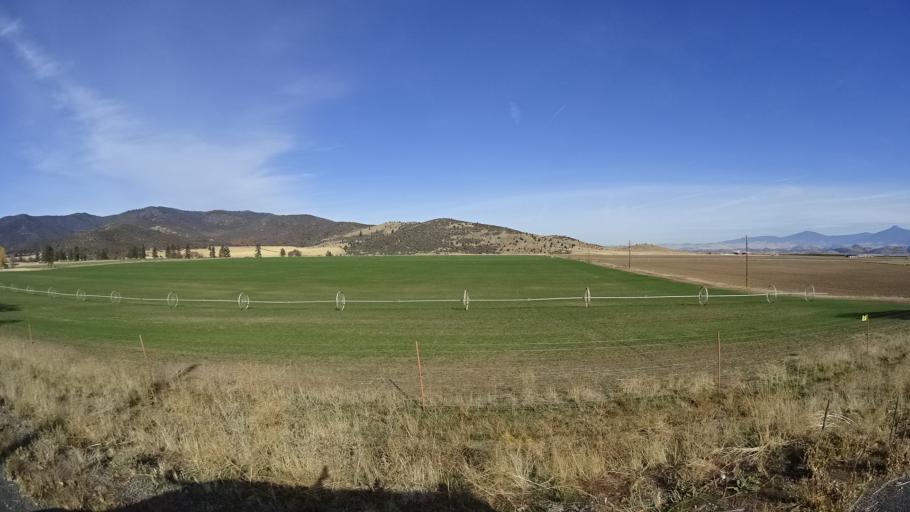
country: US
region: California
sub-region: Siskiyou County
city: Montague
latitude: 41.5393
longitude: -122.5701
